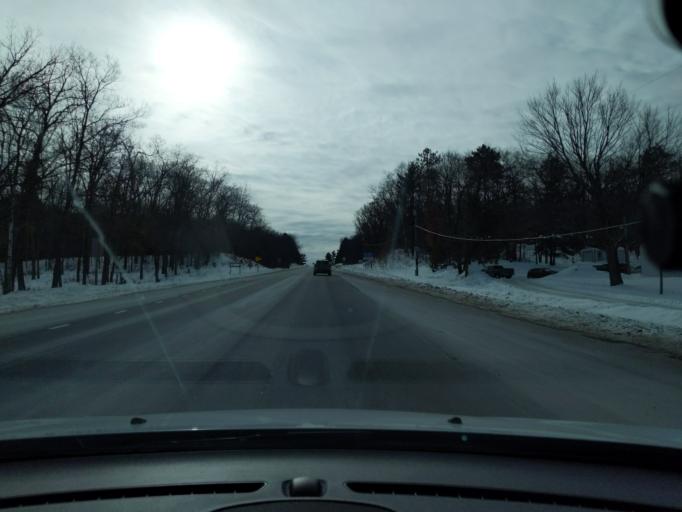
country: US
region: Wisconsin
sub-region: Washburn County
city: Spooner
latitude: 45.8074
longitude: -91.8995
